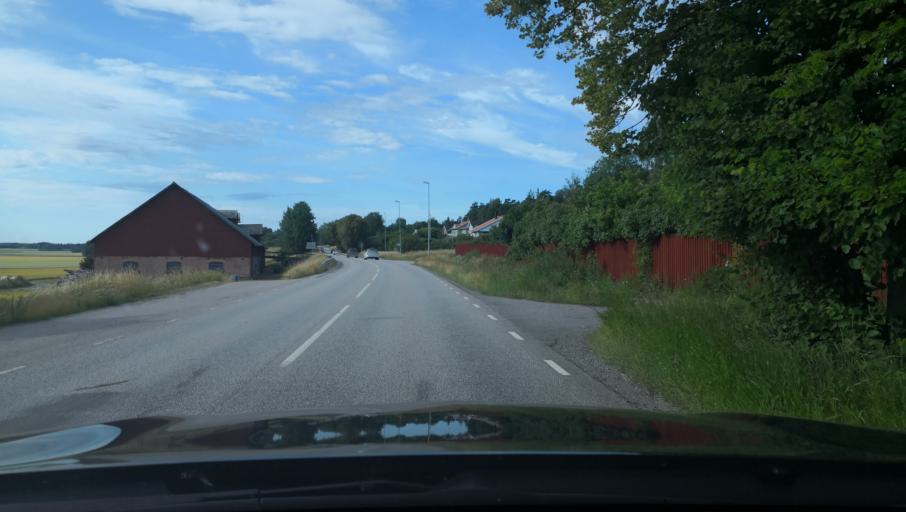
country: SE
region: Uppsala
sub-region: Habo Kommun
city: Balsta
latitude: 59.5945
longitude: 17.5108
